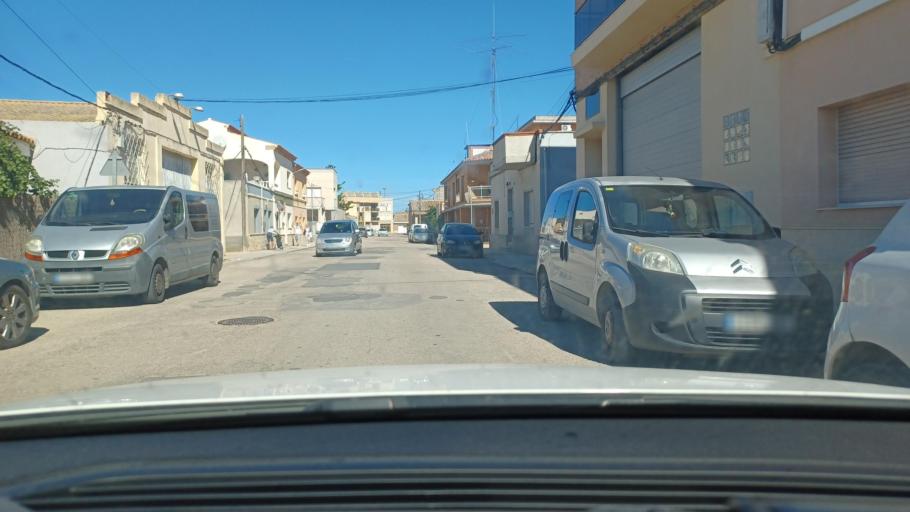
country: ES
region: Catalonia
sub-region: Provincia de Tarragona
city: Deltebre
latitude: 40.7187
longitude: 0.7397
